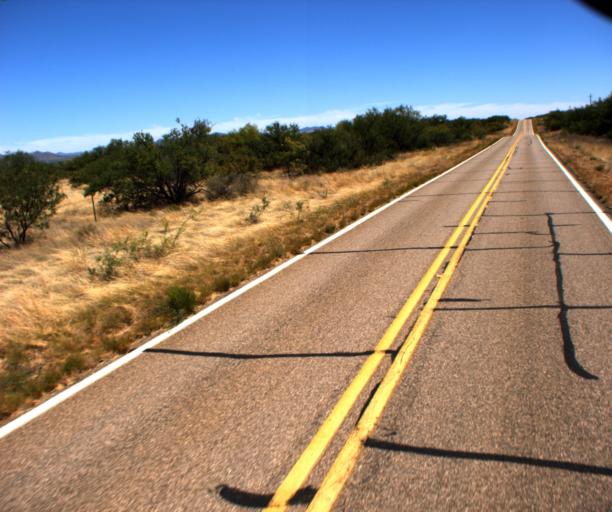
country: US
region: Arizona
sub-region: Pima County
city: Three Points
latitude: 31.7165
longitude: -111.4878
